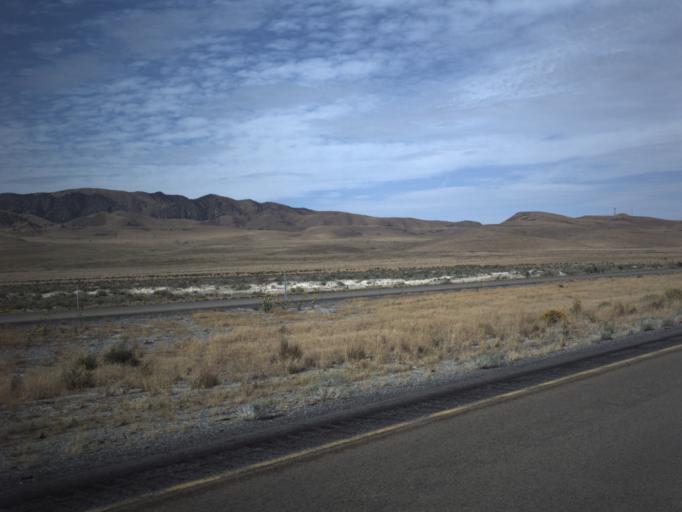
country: US
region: Utah
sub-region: Tooele County
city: Grantsville
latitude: 40.7862
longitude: -112.8238
